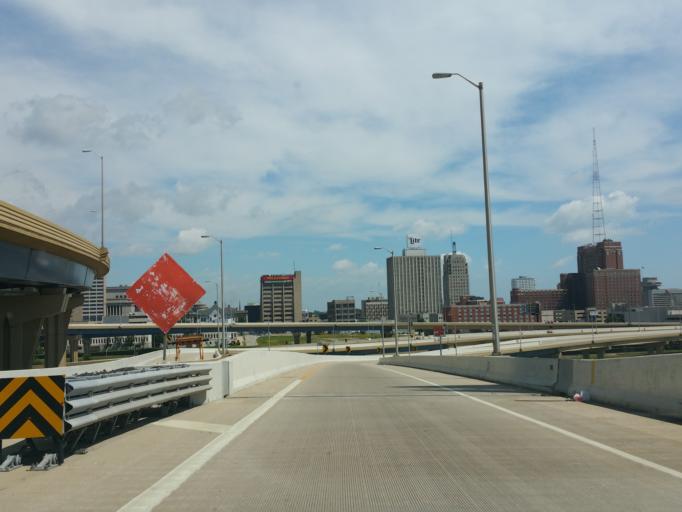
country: US
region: Wisconsin
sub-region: Milwaukee County
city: Milwaukee
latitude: 43.0324
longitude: -87.9221
